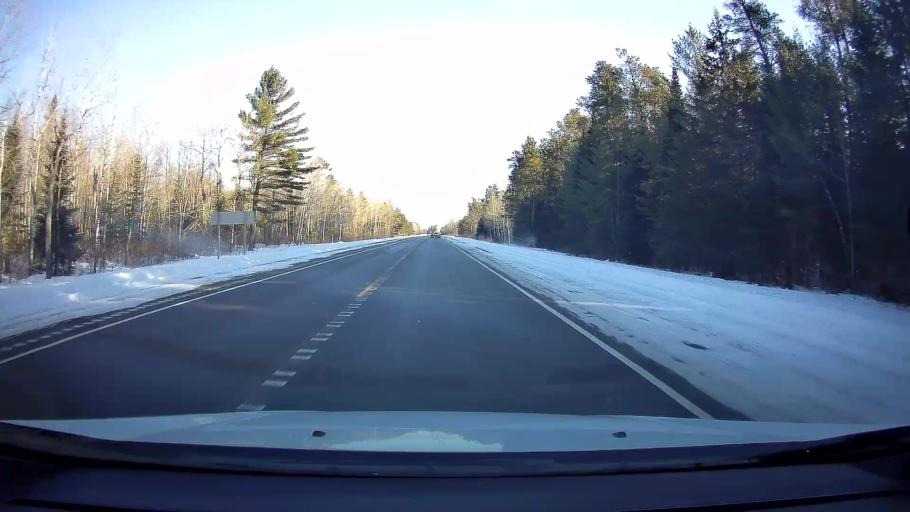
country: US
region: Wisconsin
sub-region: Sawyer County
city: Hayward
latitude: 46.0869
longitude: -91.3944
